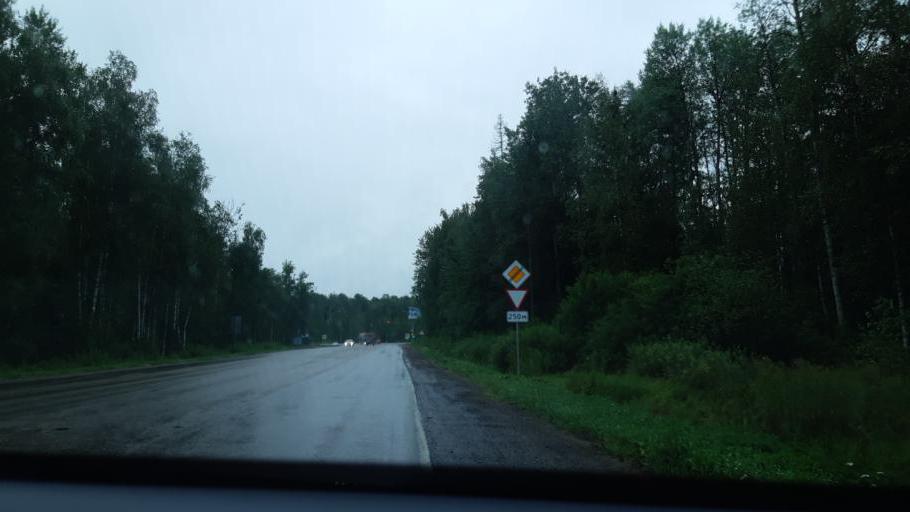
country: RU
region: Smolensk
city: Gagarin
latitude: 55.5021
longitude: 35.0363
